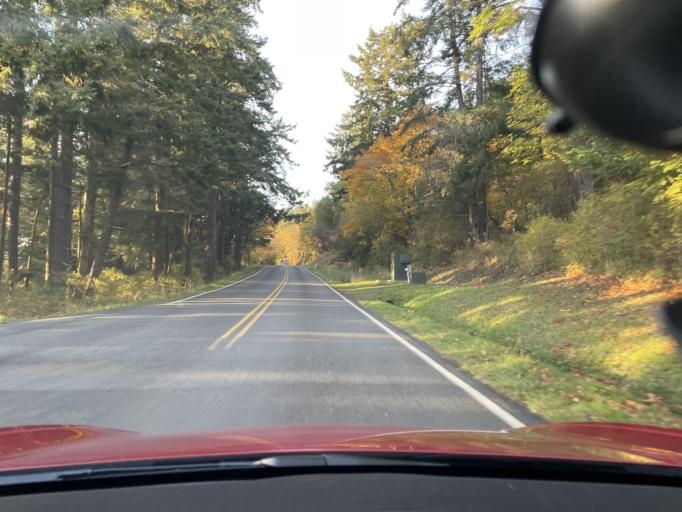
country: US
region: Washington
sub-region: San Juan County
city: Friday Harbor
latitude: 48.5786
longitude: -123.1425
